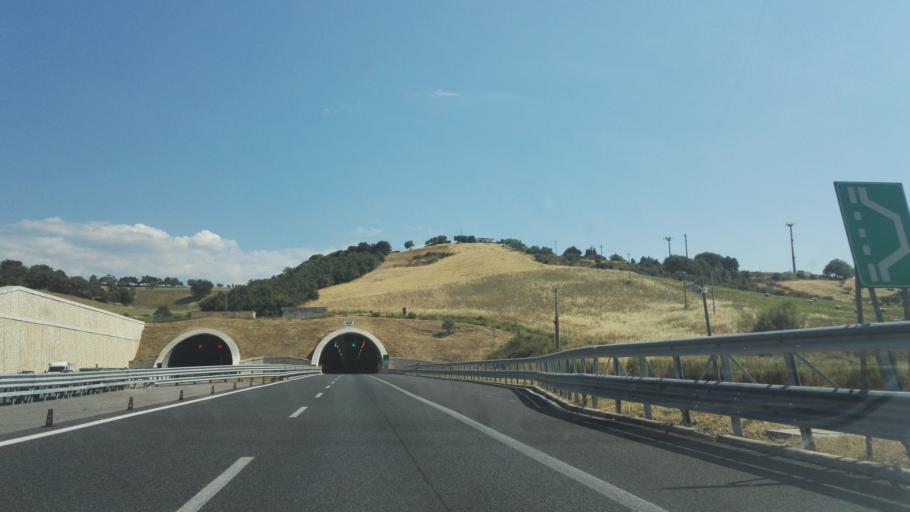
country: IT
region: Calabria
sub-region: Provincia di Cosenza
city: Tarsia
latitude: 39.6121
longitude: 16.2308
